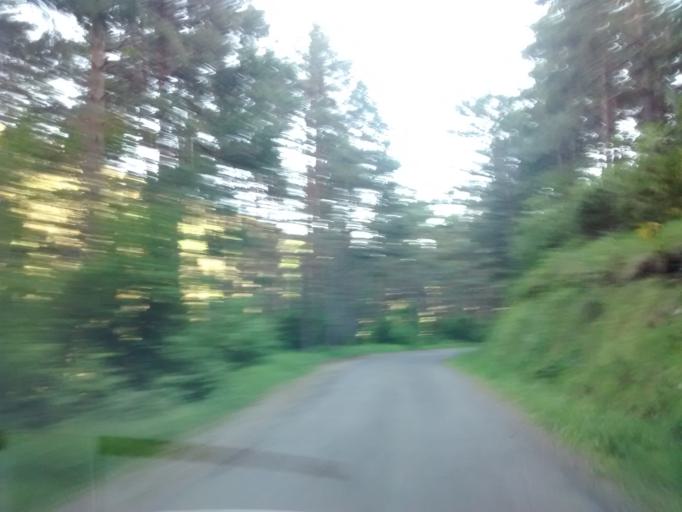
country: ES
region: Aragon
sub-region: Provincia de Huesca
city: Borau
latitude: 42.7106
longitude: -0.6092
